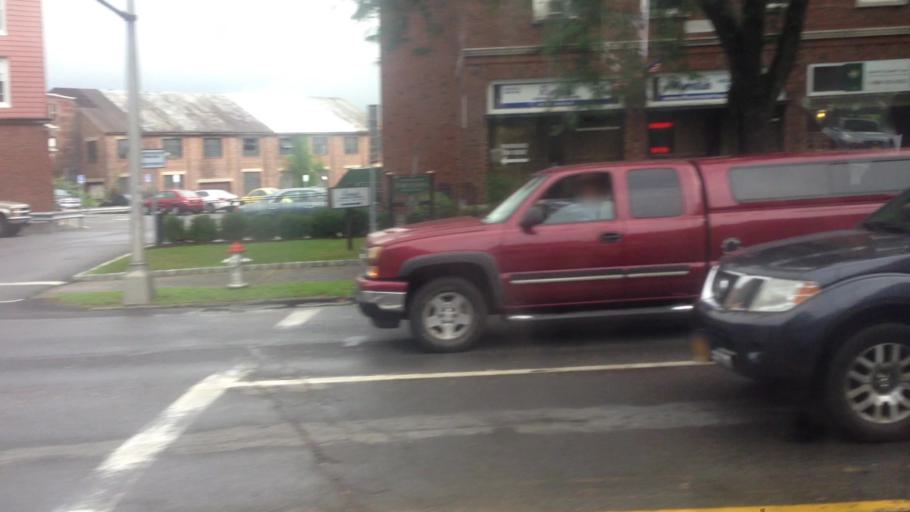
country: US
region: New York
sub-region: Ulster County
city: Kingston
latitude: 41.9325
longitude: -74.0155
